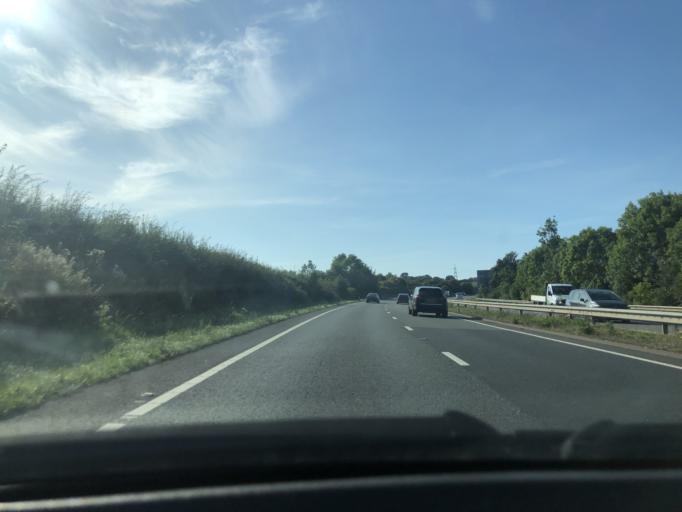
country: GB
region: England
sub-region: Devon
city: Exeter
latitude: 50.7062
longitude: -3.5603
